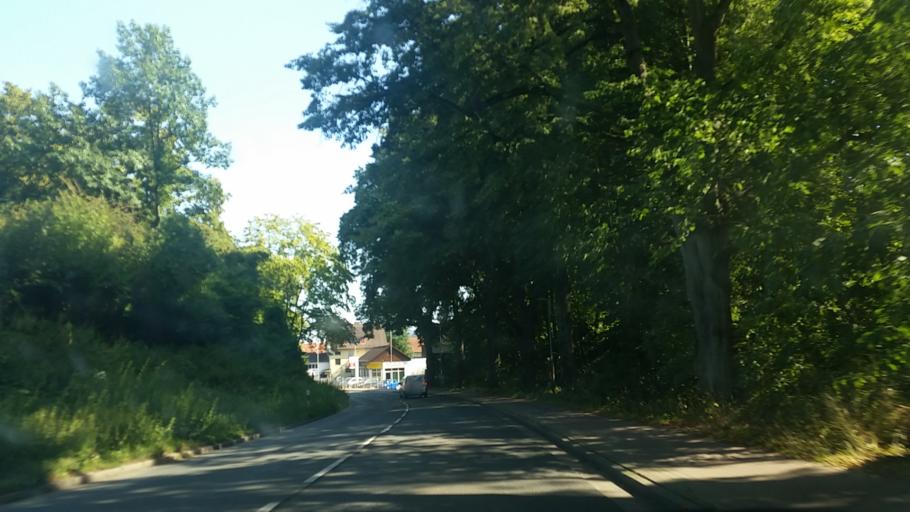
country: DE
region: Lower Saxony
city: Coppenbrugge
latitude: 52.1186
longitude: 9.5393
